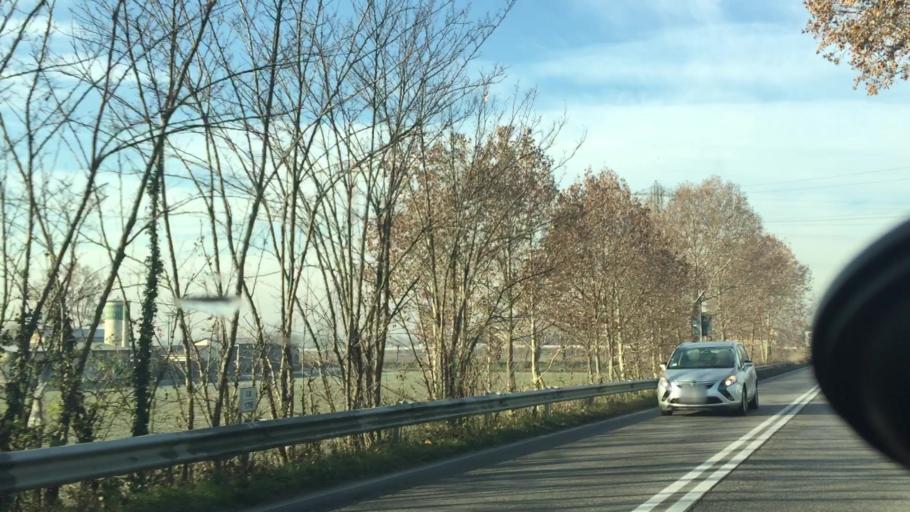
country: IT
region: Lombardy
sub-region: Provincia di Bergamo
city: Geromina
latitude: 45.5233
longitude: 9.5638
